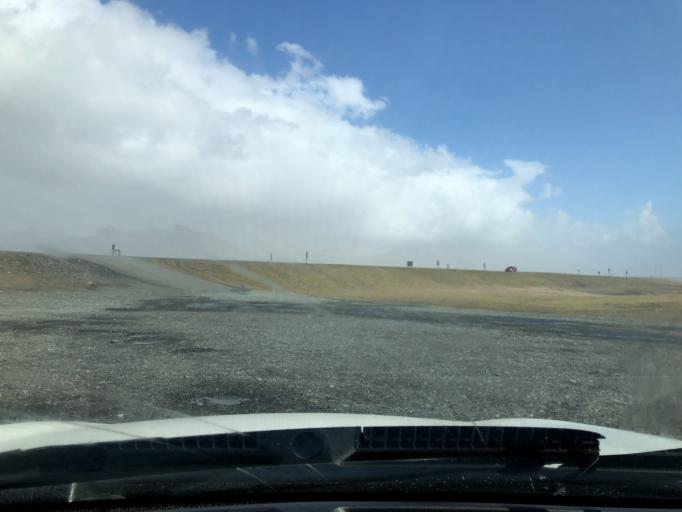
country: IS
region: East
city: Hoefn
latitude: 64.0454
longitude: -16.1777
